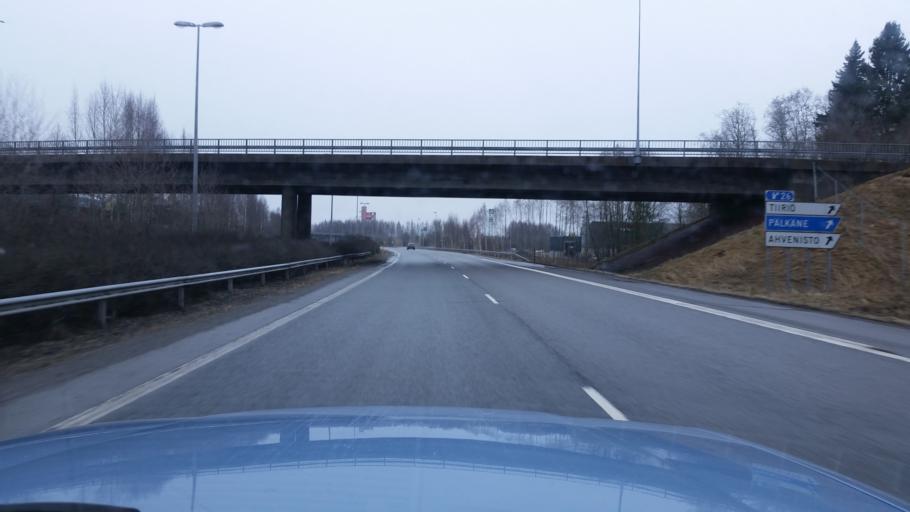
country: FI
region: Haeme
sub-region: Haemeenlinna
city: Haemeenlinna
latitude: 61.0156
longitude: 24.4113
